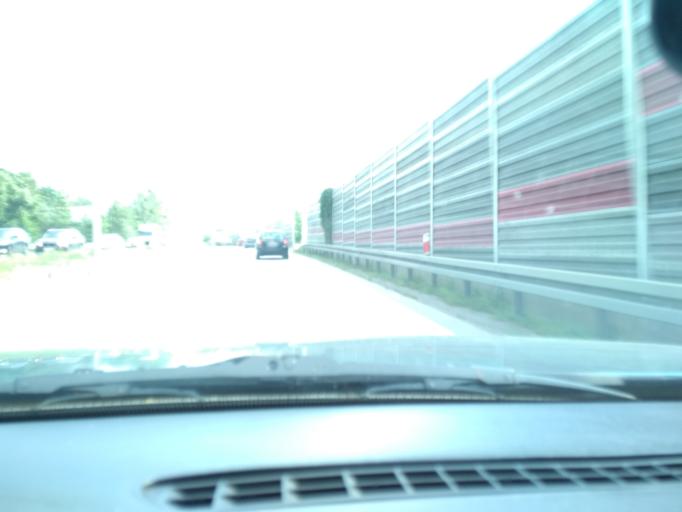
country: PL
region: Silesian Voivodeship
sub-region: Zory
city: Zory
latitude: 50.0174
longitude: 18.7074
